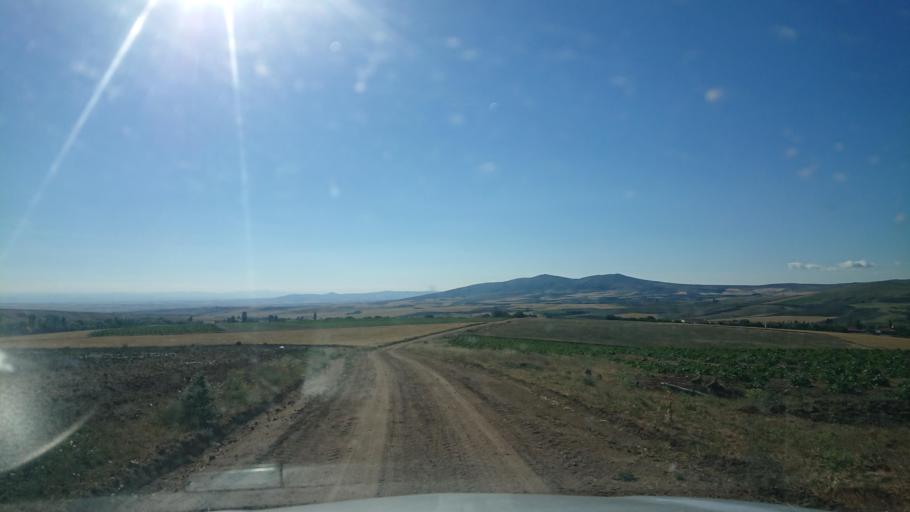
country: TR
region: Aksaray
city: Agacoren
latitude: 38.8290
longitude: 33.9497
